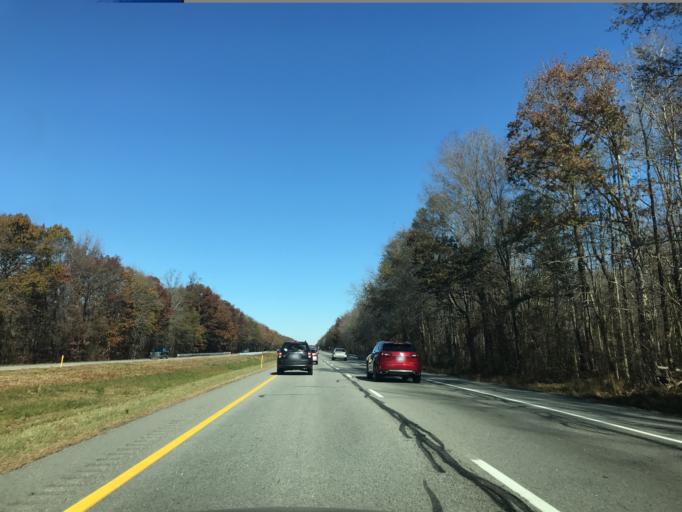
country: US
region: Delaware
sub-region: New Castle County
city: Townsend
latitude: 39.2987
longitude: -75.8520
